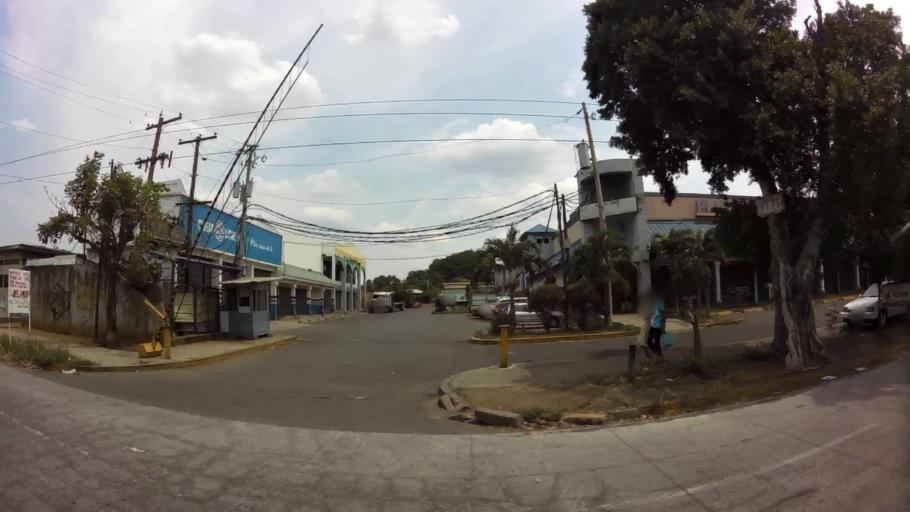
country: NI
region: Managua
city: Managua
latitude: 12.1576
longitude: -86.2917
